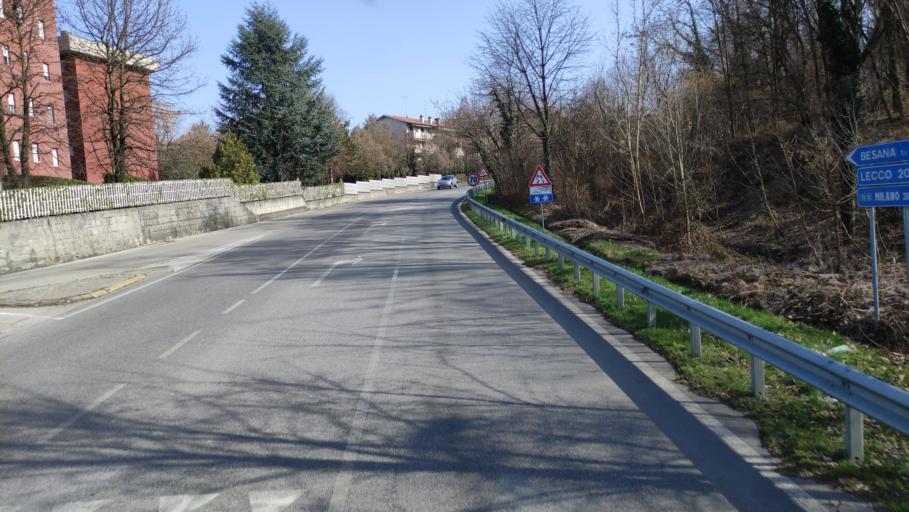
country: IT
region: Lombardy
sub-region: Provincia di Monza e Brianza
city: Capriano
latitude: 45.7319
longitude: 9.2601
